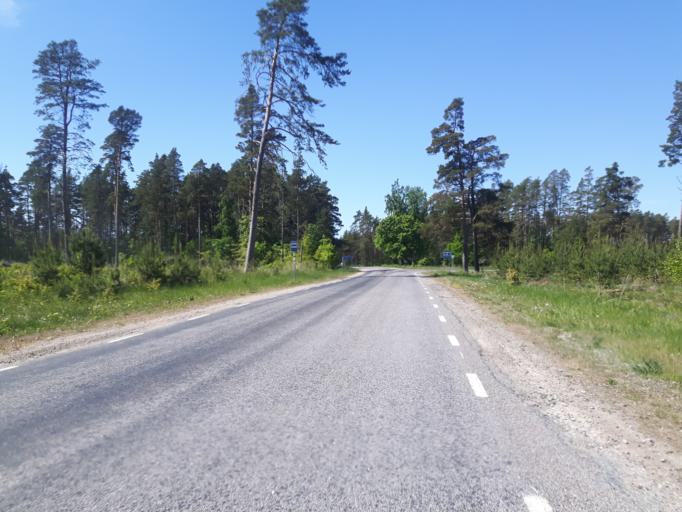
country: EE
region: Laeaene-Virumaa
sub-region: Viru-Nigula vald
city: Kunda
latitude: 59.4970
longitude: 26.4855
